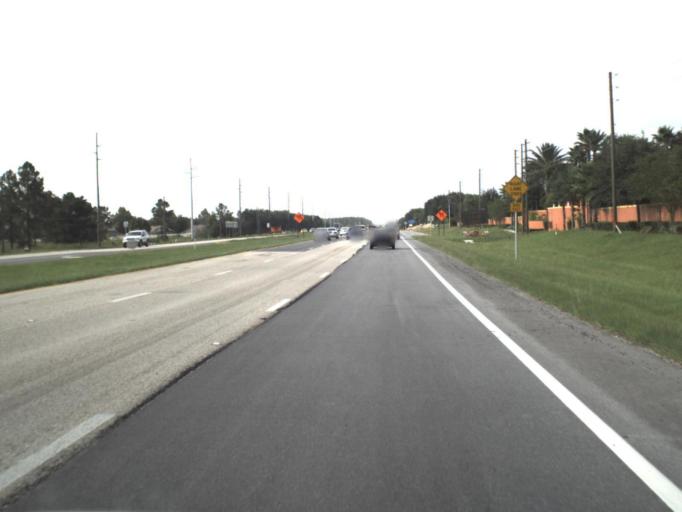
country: US
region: Florida
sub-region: Lake County
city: Four Corners
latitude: 28.2854
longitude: -81.6635
